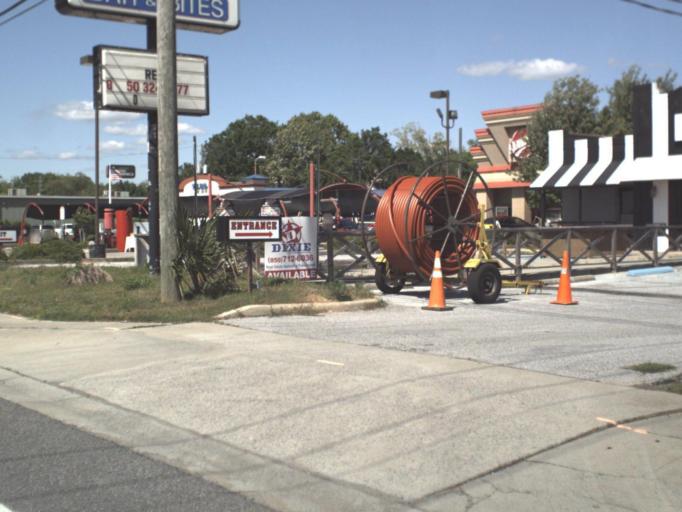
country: US
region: Florida
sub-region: Escambia County
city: Ferry Pass
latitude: 30.4977
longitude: -87.2217
